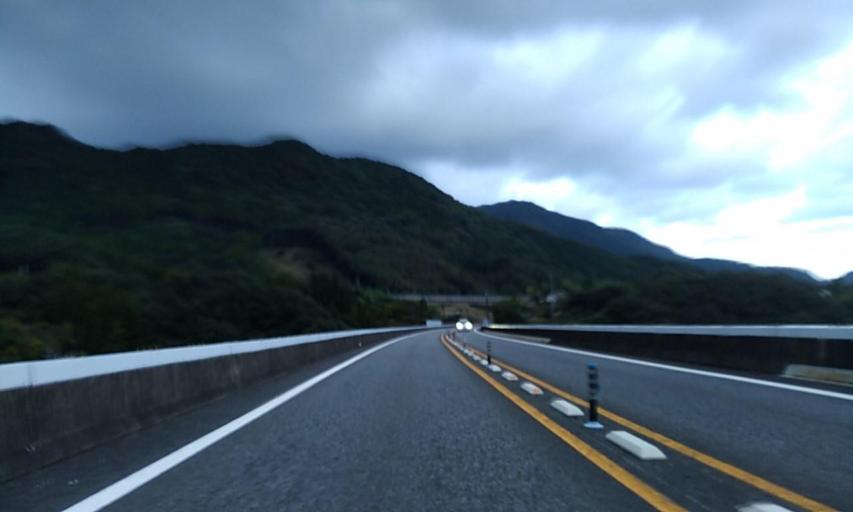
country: JP
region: Wakayama
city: Shingu
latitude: 33.6848
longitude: 135.9535
